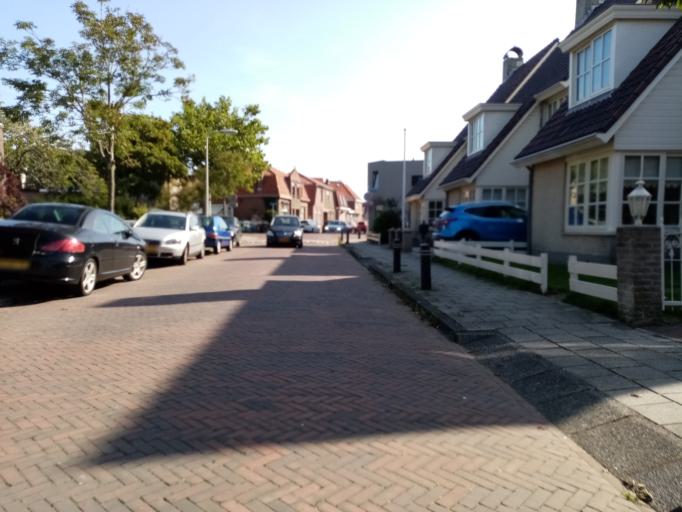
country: NL
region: South Holland
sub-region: Gemeente Noordwijk
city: Noordwijk-Binnen
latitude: 52.2335
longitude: 4.4407
